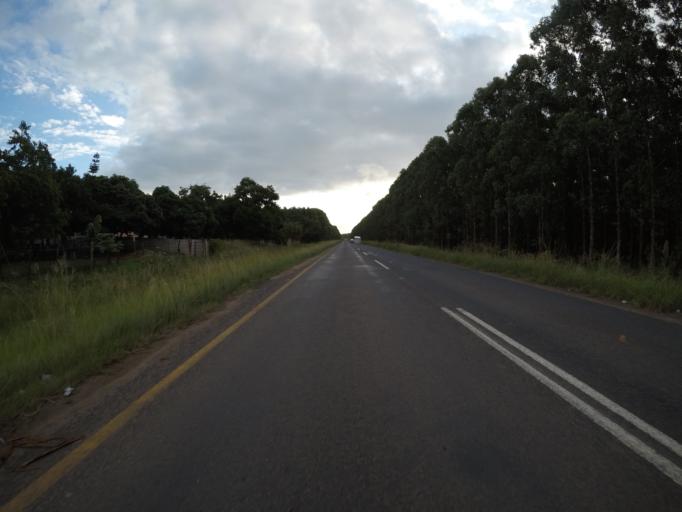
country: ZA
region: KwaZulu-Natal
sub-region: uMkhanyakude District Municipality
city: Mtubatuba
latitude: -28.3983
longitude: 32.2134
